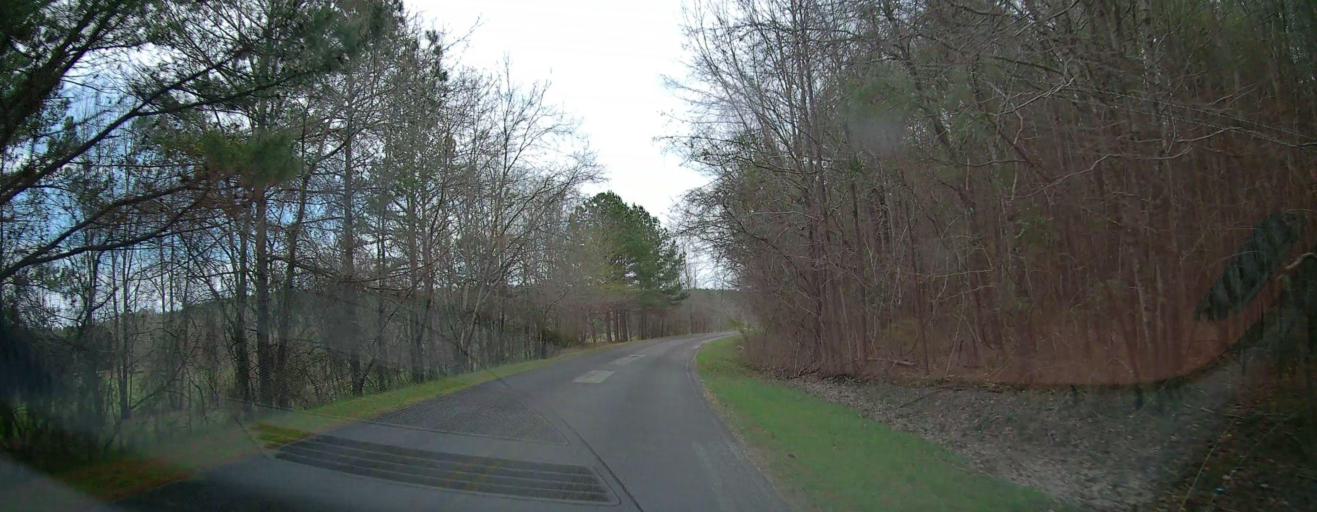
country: US
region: Alabama
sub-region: Marion County
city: Hamilton
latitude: 34.2005
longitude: -88.1716
